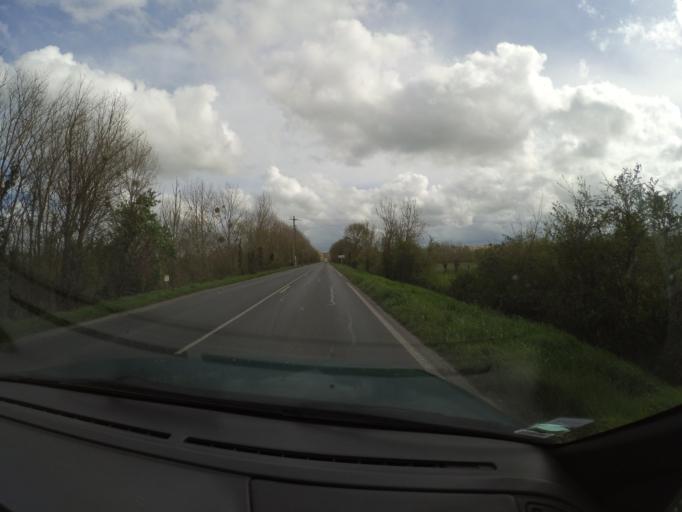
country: FR
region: Pays de la Loire
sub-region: Departement de la Loire-Atlantique
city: Ancenis
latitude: 47.3554
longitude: -1.1725
